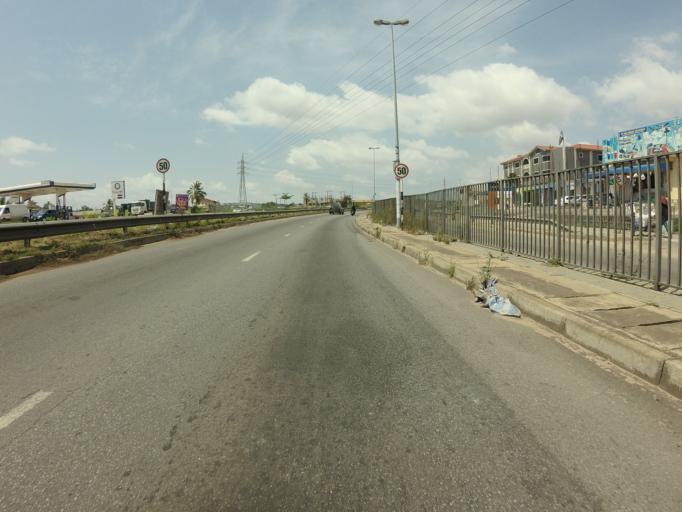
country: GH
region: Greater Accra
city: Gbawe
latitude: 5.5920
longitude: -0.2875
